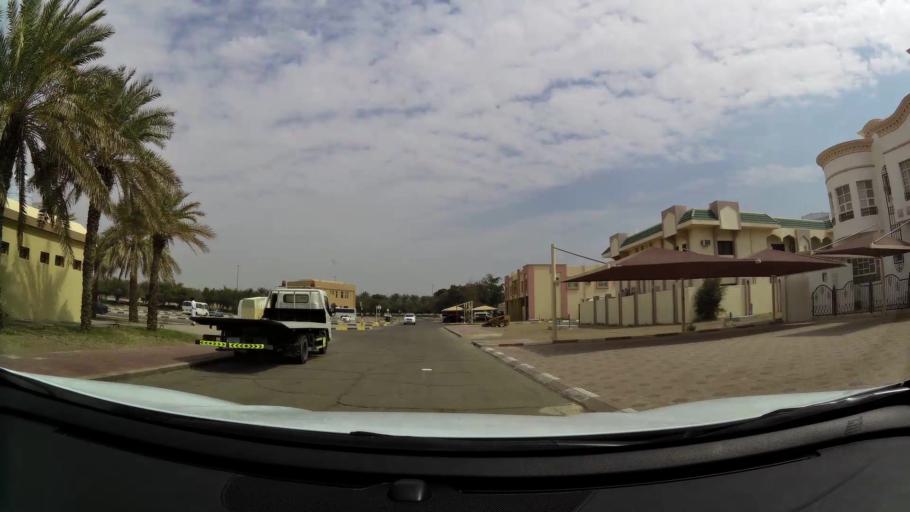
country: AE
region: Abu Dhabi
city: Al Ain
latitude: 24.2146
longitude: 55.7877
